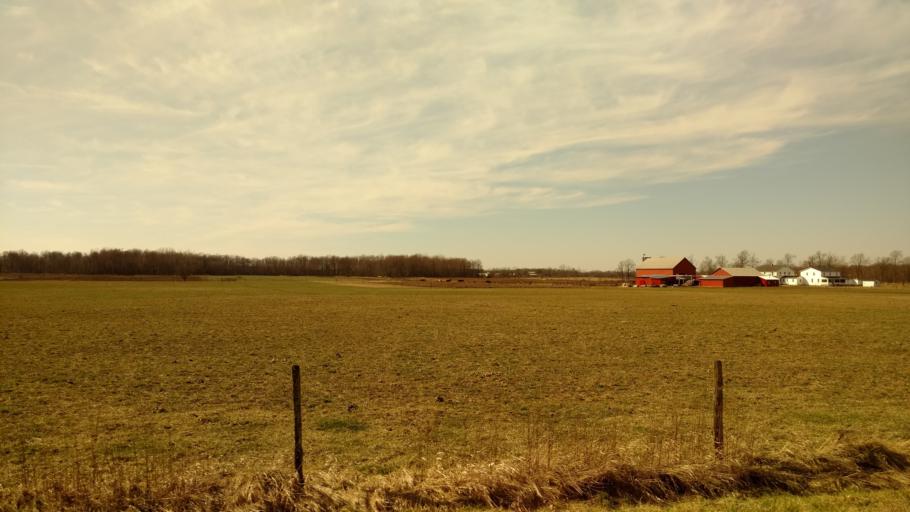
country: US
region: Ohio
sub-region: Hardin County
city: Kenton
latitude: 40.5982
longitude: -83.5040
